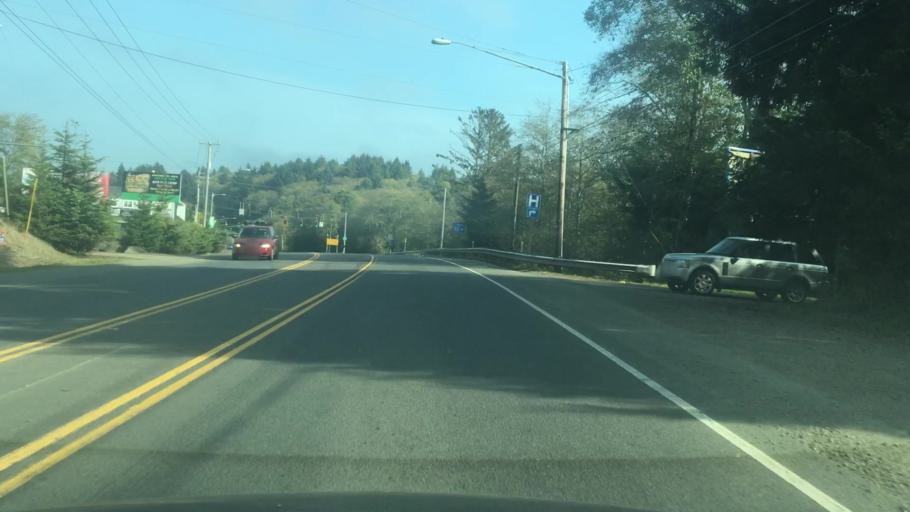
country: US
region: Oregon
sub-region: Lincoln County
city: Lincoln City
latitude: 44.9973
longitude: -123.9987
